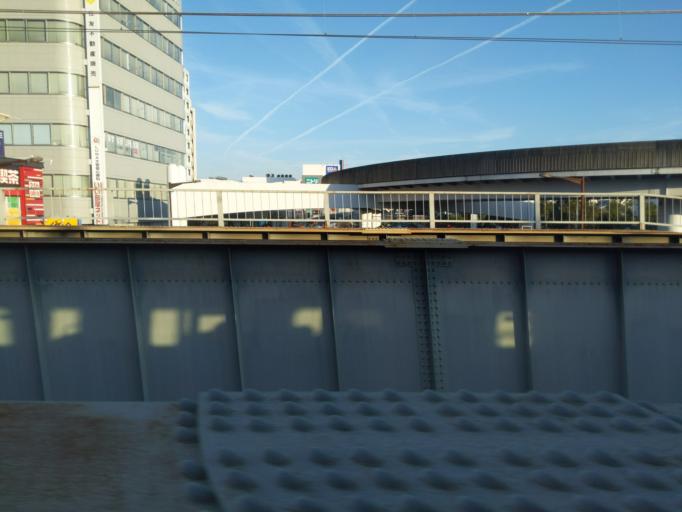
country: JP
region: Aichi
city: Nagoya-shi
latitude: 35.1923
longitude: 136.9372
